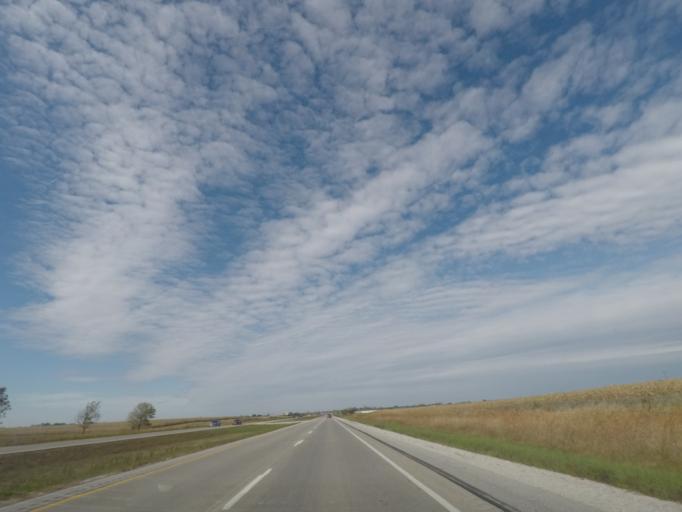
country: US
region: Iowa
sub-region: Story County
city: Ames
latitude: 42.0162
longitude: -93.7041
